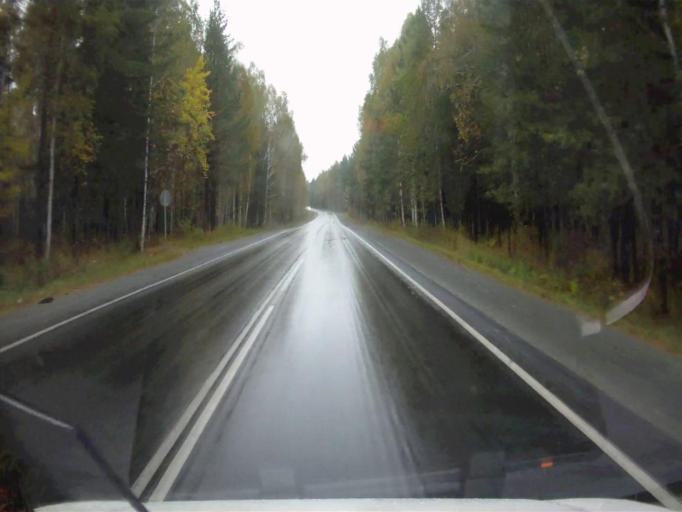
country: RU
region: Chelyabinsk
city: Tayginka
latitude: 55.5914
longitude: 60.6270
